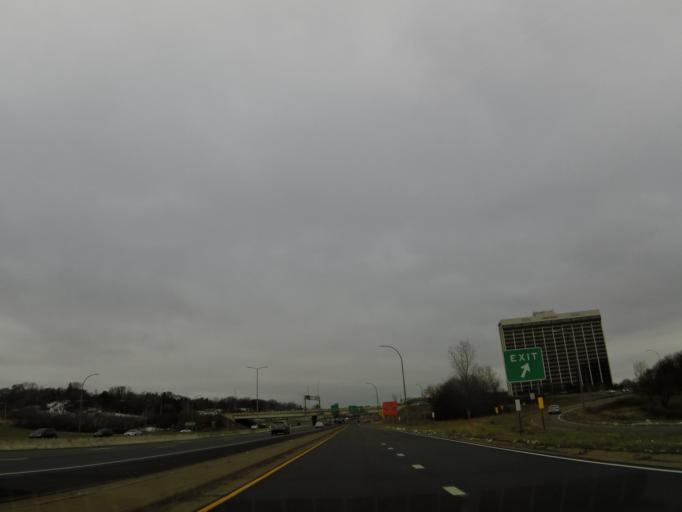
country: US
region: Minnesota
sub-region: Hennepin County
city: Saint Louis Park
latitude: 44.9739
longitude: -93.3970
